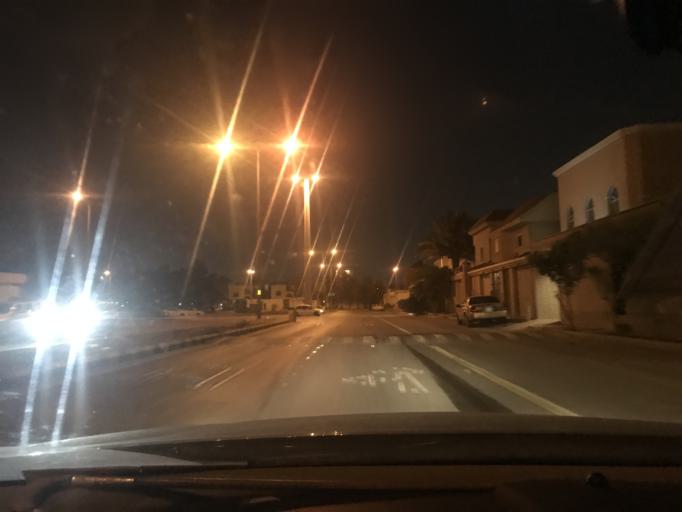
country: SA
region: Ar Riyad
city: Riyadh
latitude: 24.7588
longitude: 46.7447
